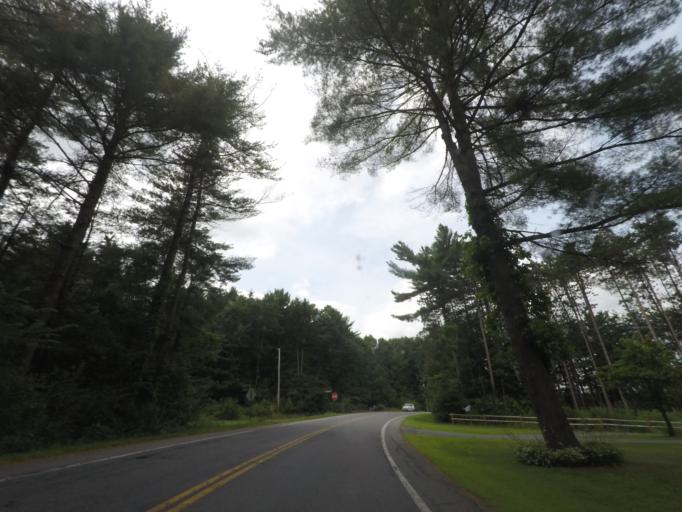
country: US
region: New York
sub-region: Saratoga County
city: Saratoga Springs
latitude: 43.0503
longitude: -73.6848
